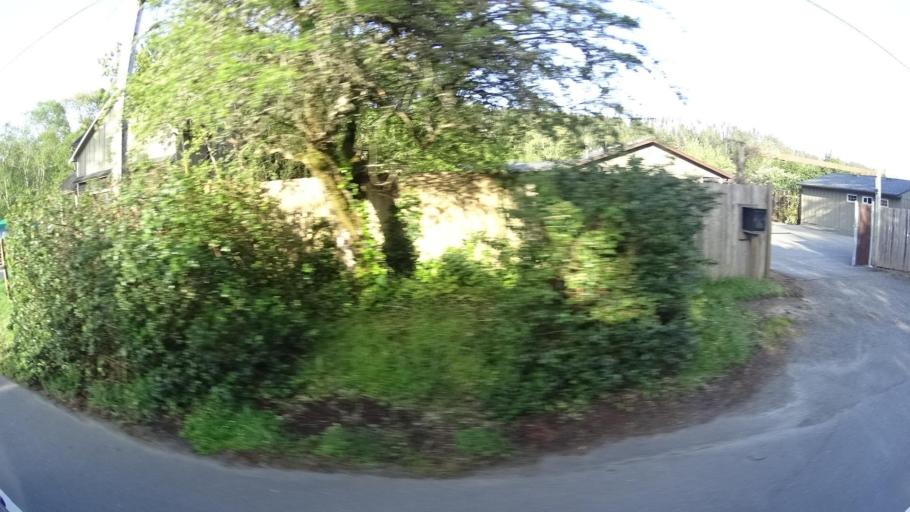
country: US
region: California
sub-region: Humboldt County
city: Myrtletown
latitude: 40.7670
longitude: -124.0682
